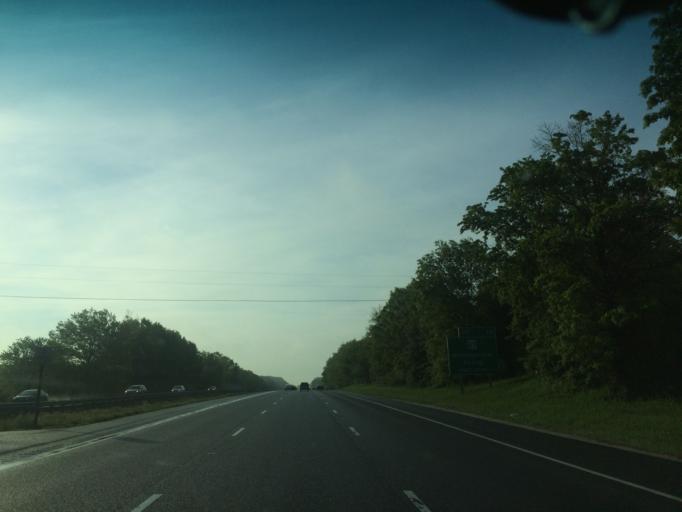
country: US
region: Maryland
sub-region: Carroll County
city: Sykesville
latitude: 39.3312
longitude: -77.0288
